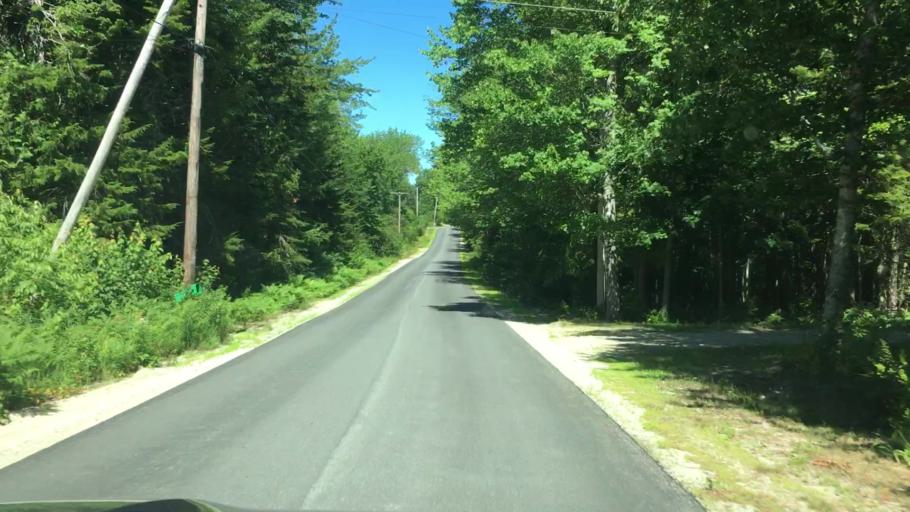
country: US
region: Maine
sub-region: Hancock County
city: Sedgwick
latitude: 44.3194
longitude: -68.6274
